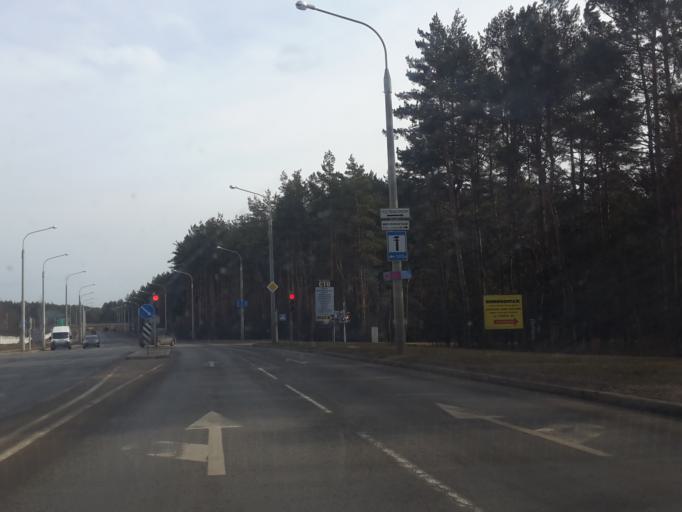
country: BY
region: Minsk
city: Vyaliki Trastsyanets
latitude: 53.9017
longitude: 27.6808
